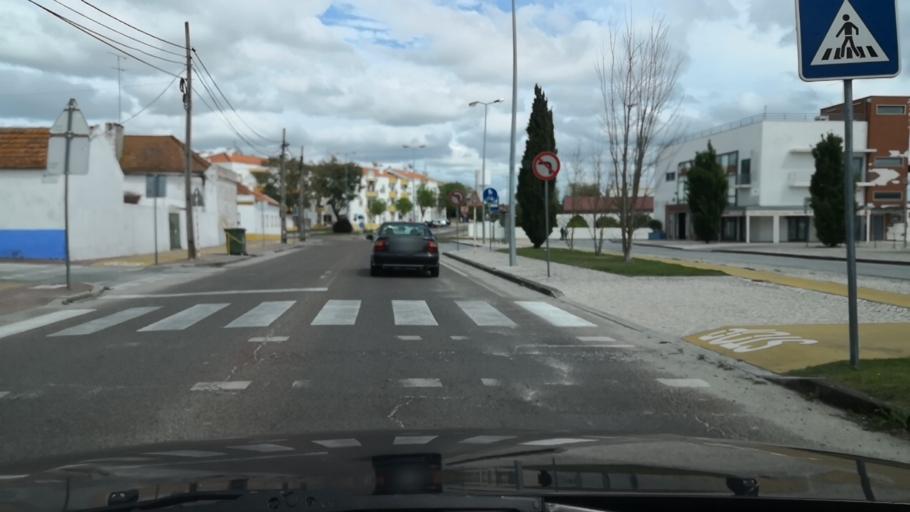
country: PT
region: Evora
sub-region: Vendas Novas
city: Vendas Novas
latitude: 38.6747
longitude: -8.4581
